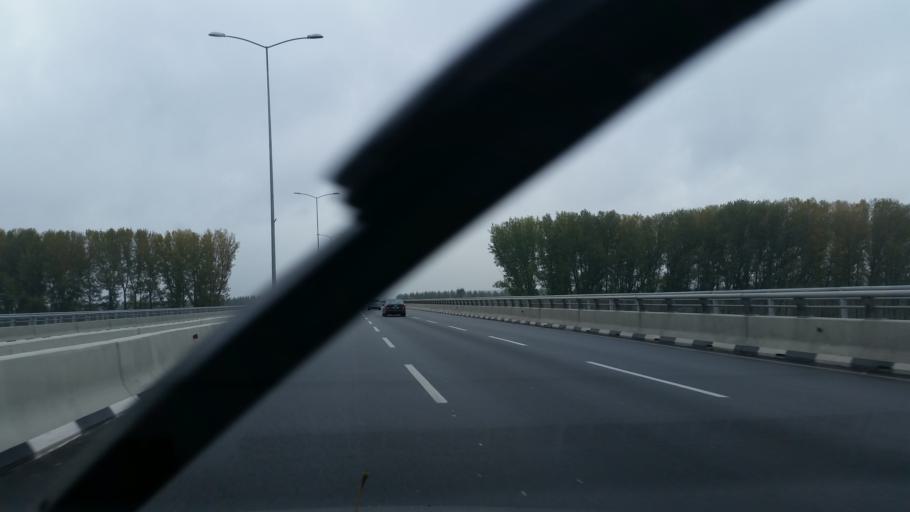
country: RS
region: Central Serbia
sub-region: Belgrade
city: Zemun
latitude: 44.8659
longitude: 20.3823
